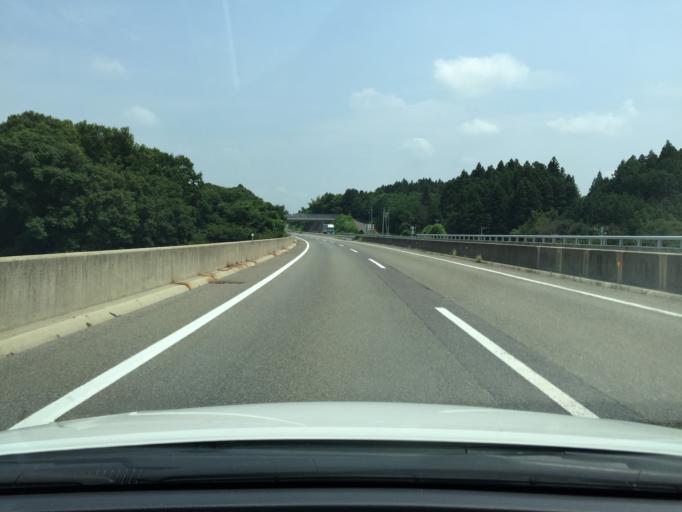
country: JP
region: Fukushima
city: Koriyama
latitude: 37.4429
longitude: 140.4244
